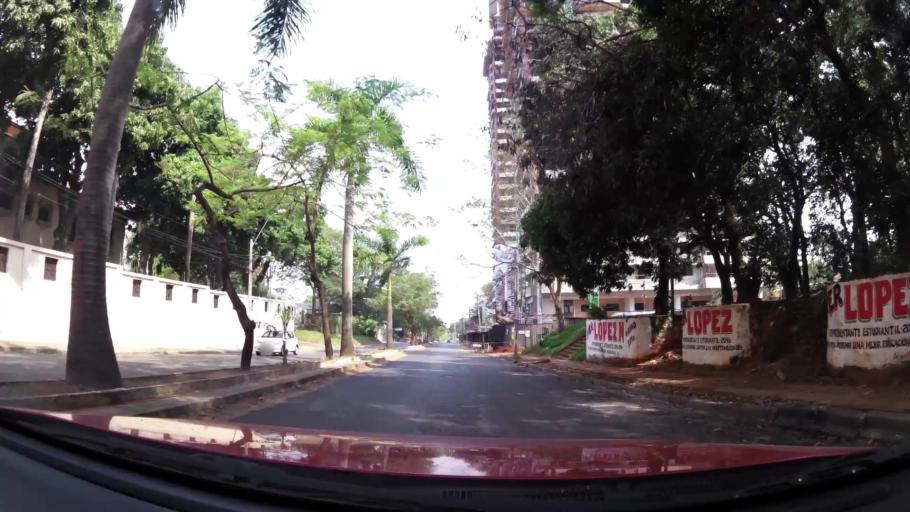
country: PY
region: Asuncion
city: Asuncion
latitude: -25.2630
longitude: -57.5735
